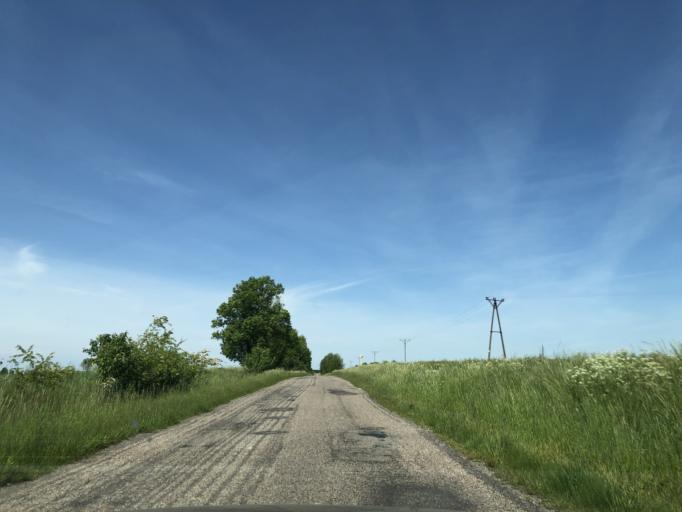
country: PL
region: West Pomeranian Voivodeship
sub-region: Powiat kolobrzeski
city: Goscino
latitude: 53.9871
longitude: 15.7116
